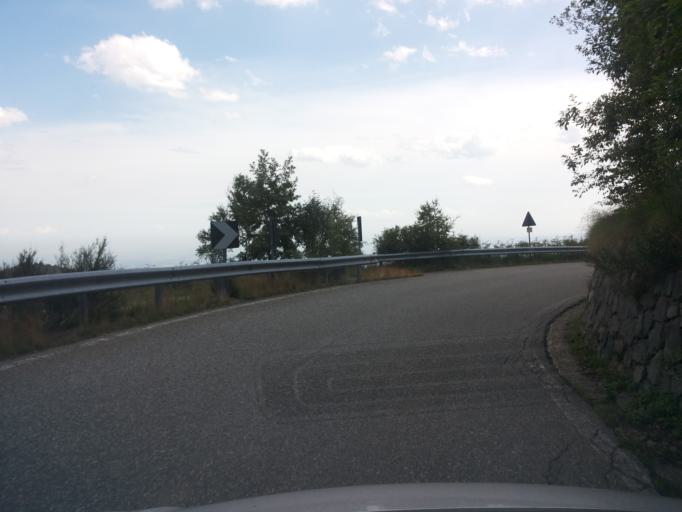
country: IT
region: Piedmont
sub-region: Provincia di Biella
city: Sagliano Micca
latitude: 45.6602
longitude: 8.0580
